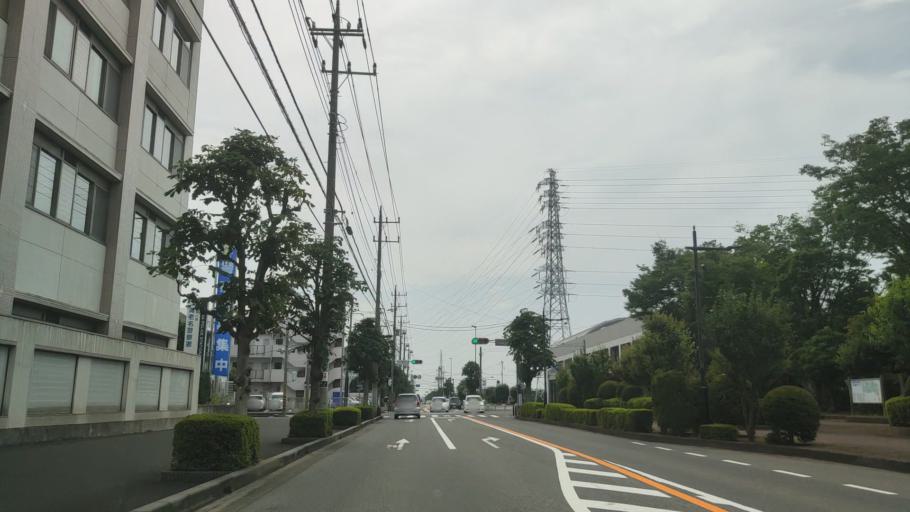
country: JP
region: Kanagawa
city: Atsugi
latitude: 35.4457
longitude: 139.3914
